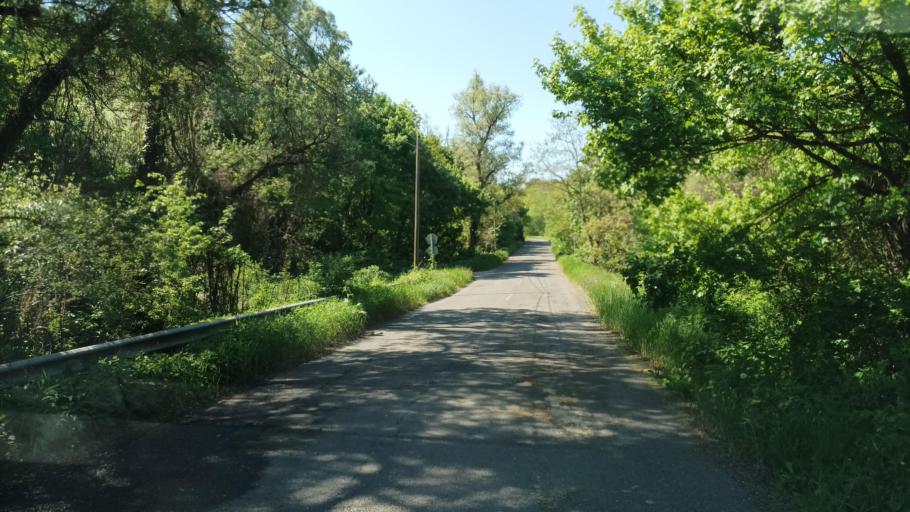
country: HU
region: Pest
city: Uri
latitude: 47.3998
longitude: 19.4917
